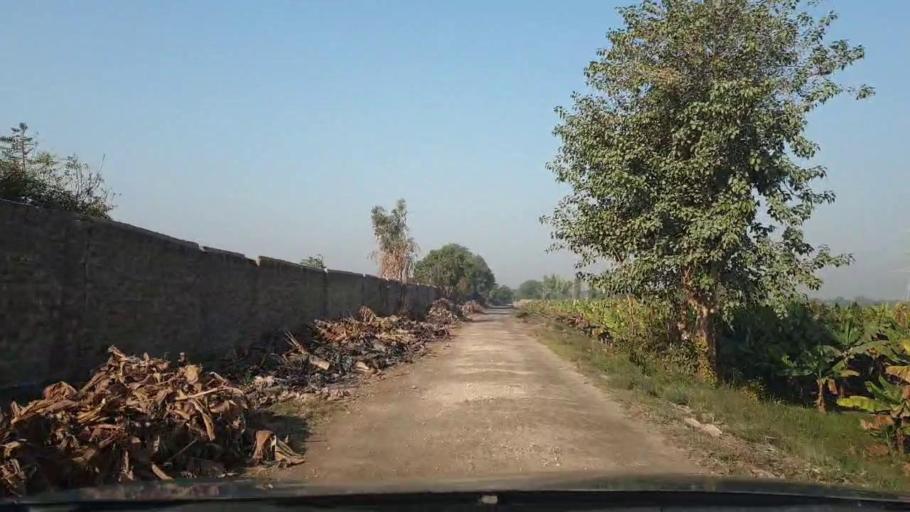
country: PK
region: Sindh
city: Tando Allahyar
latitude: 25.4916
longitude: 68.7130
